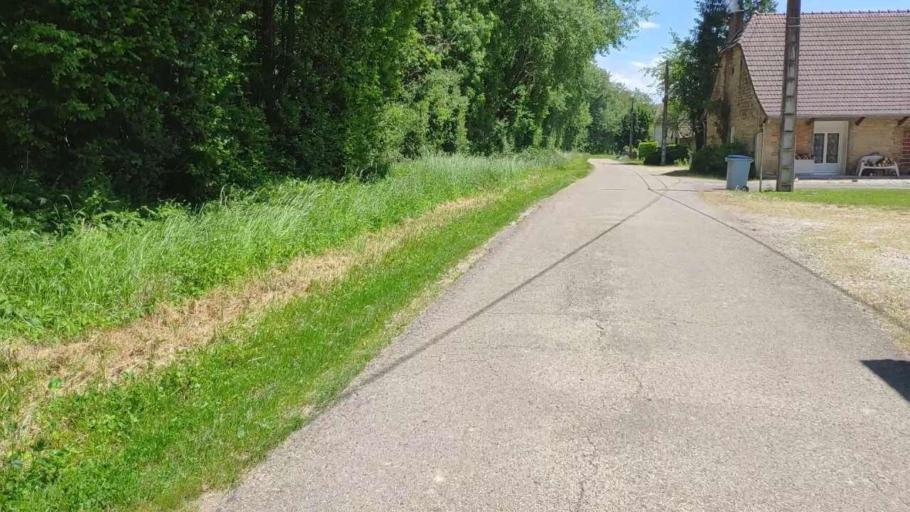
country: FR
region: Franche-Comte
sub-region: Departement du Jura
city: Bletterans
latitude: 46.7892
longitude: 5.4429
